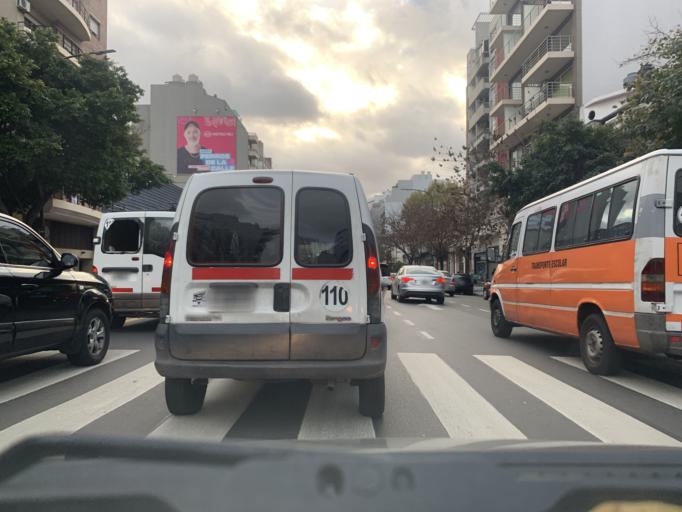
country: AR
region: Buenos Aires F.D.
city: Colegiales
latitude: -34.5789
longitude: -58.4560
